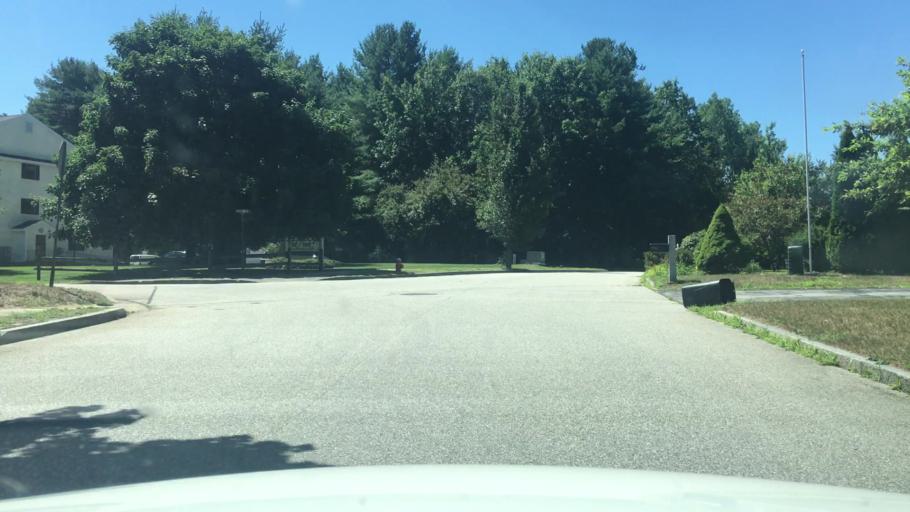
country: US
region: New Hampshire
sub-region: Merrimack County
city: Boscawen
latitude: 43.2713
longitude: -71.5994
